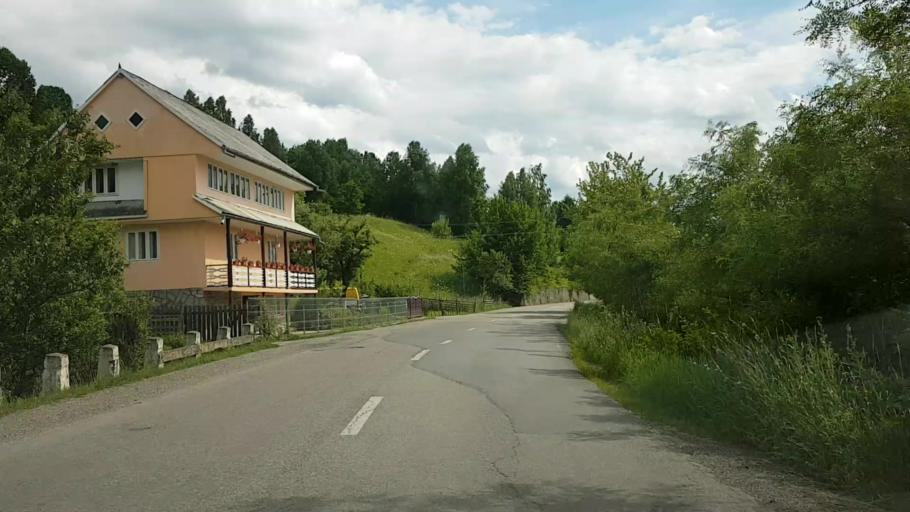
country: RO
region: Neamt
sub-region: Comuna Hangu
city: Hangu
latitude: 47.0325
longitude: 26.0666
